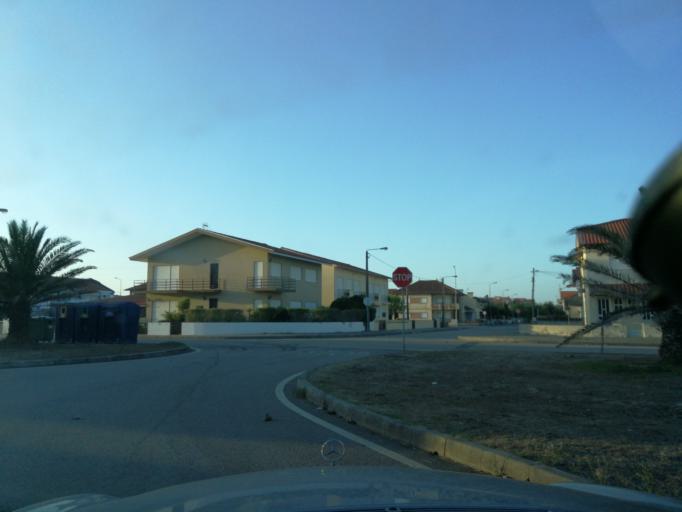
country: PT
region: Aveiro
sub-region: Murtosa
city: Murtosa
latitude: 40.7584
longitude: -8.7086
